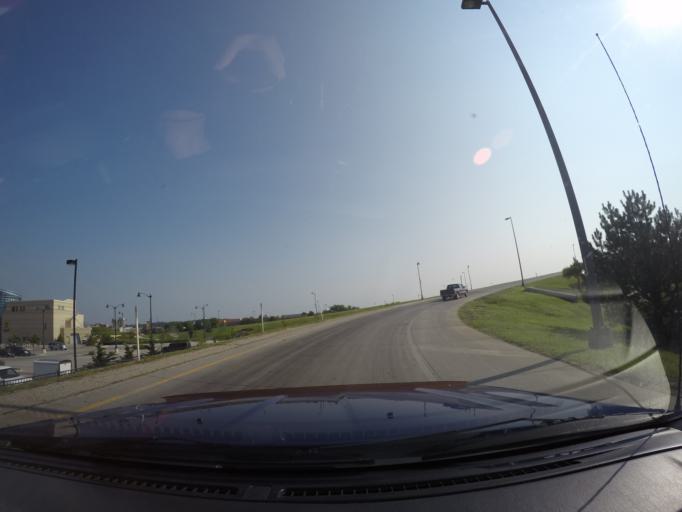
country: US
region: Kansas
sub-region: Riley County
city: Manhattan
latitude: 39.1753
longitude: -96.5587
